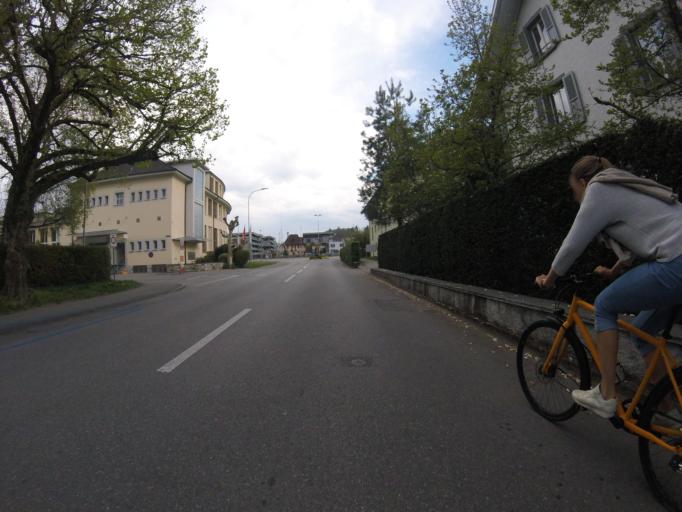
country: CH
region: Fribourg
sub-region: See District
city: Murten
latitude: 46.9255
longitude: 7.1130
